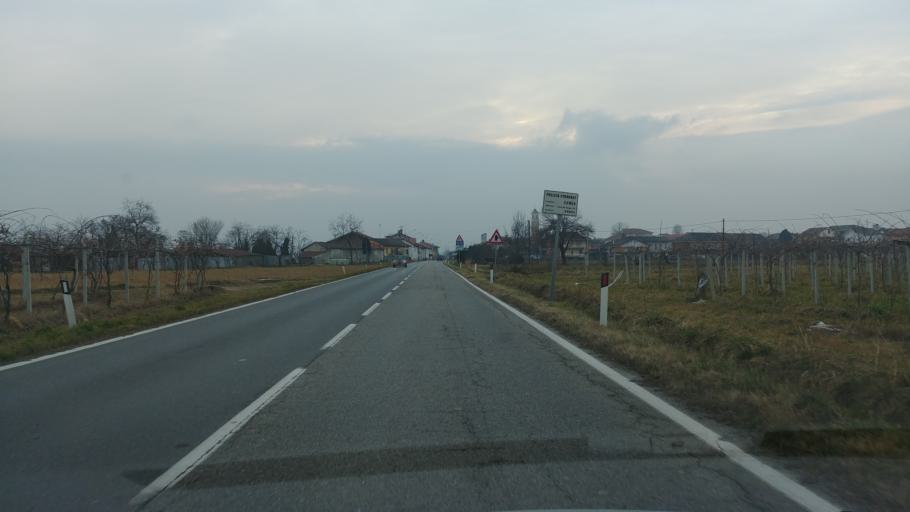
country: IT
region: Piedmont
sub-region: Provincia di Cuneo
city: Castelletto Stura
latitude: 44.4359
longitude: 7.5931
